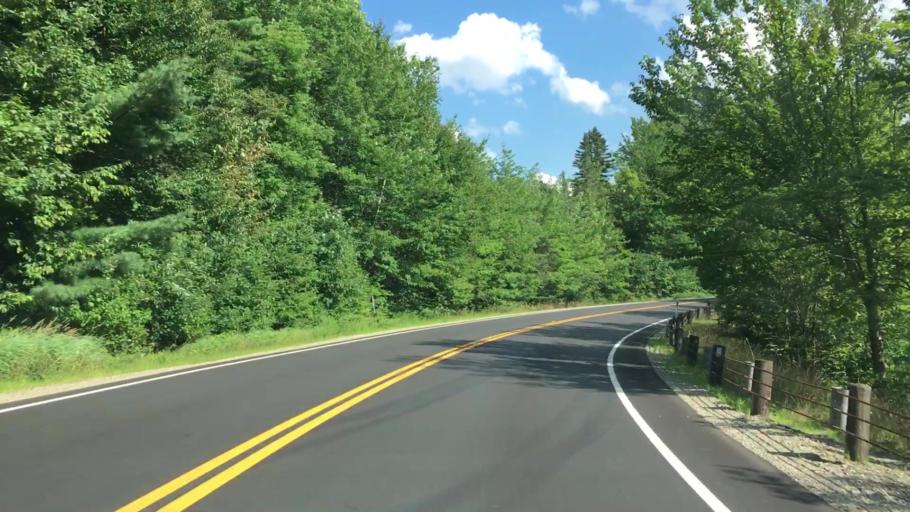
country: US
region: New Hampshire
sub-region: Grafton County
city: North Haverhill
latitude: 44.1056
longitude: -71.8673
